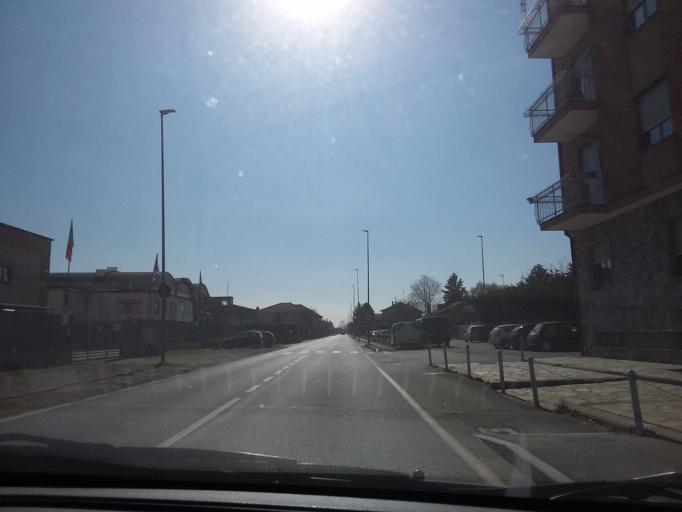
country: IT
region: Piedmont
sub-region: Provincia di Torino
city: Tetti Neirotti
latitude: 45.0585
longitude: 7.5395
